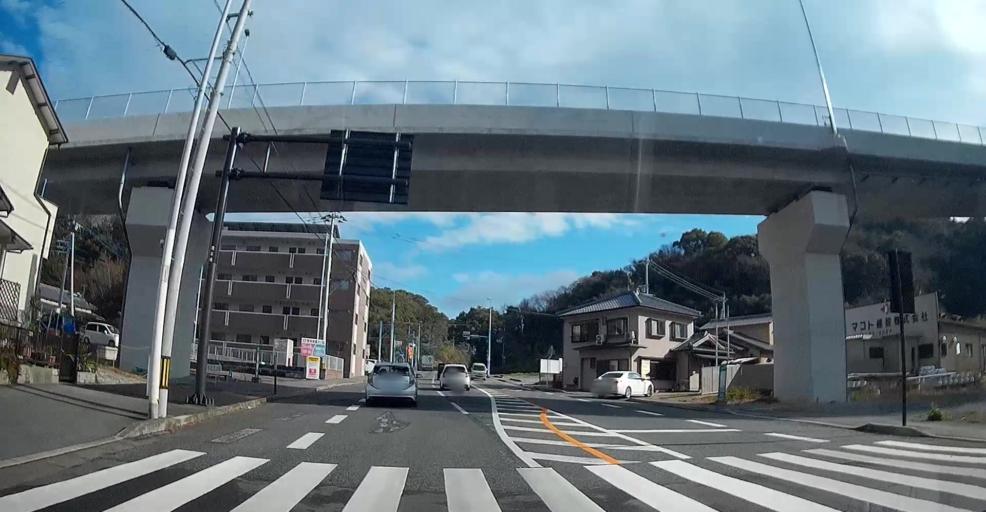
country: JP
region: Kumamoto
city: Yatsushiro
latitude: 32.6103
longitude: 130.4658
